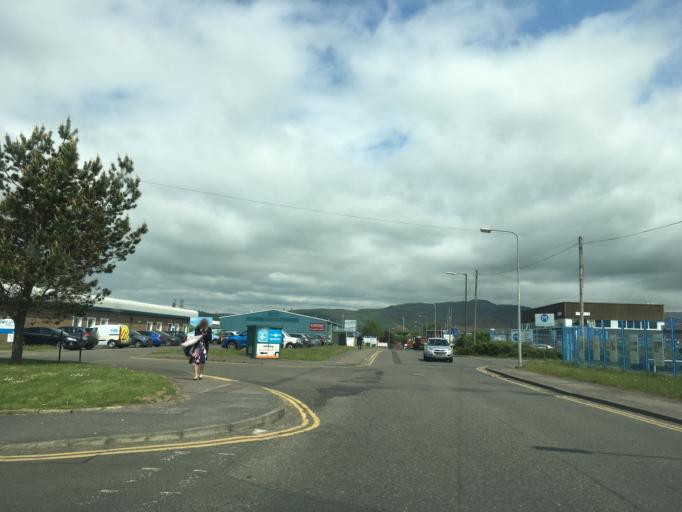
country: GB
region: Scotland
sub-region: Stirling
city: Stirling
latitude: 56.1123
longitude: -3.9150
